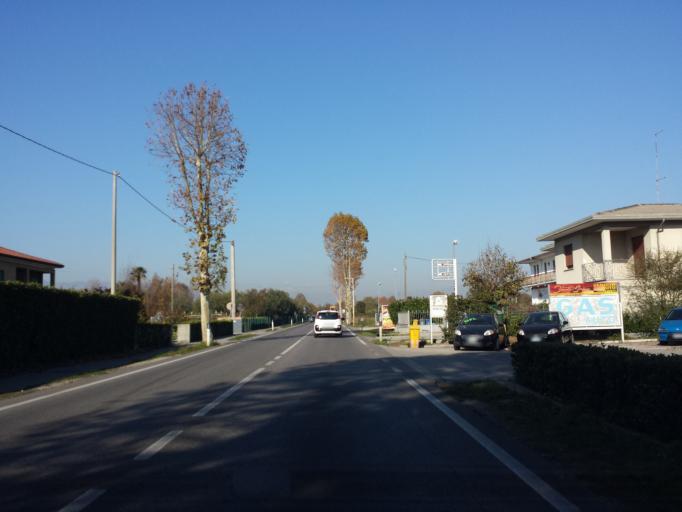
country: IT
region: Veneto
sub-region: Provincia di Treviso
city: Valla
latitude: 45.6913
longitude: 11.9276
